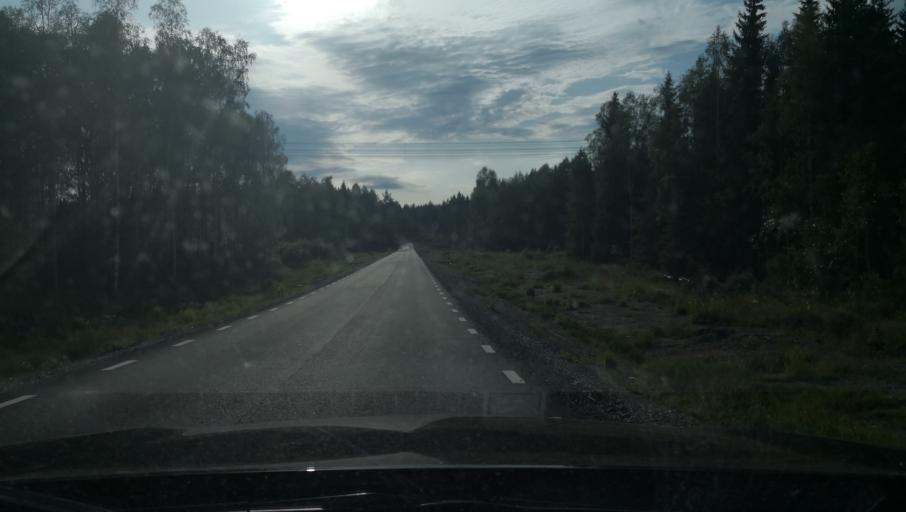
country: SE
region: Dalarna
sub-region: Smedjebackens Kommun
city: Smedjebacken
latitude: 60.0395
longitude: 15.3183
